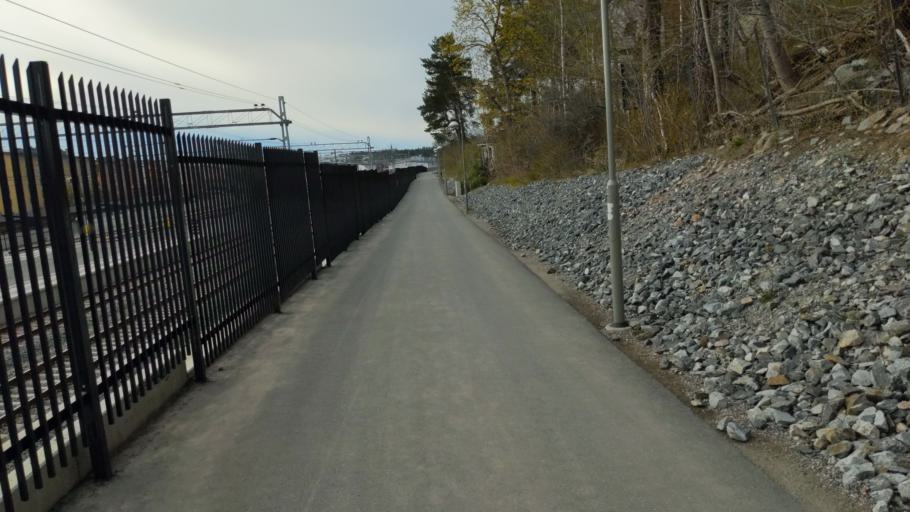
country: SE
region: Stockholm
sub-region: Stockholms Kommun
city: Kista
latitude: 59.3847
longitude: 17.8965
